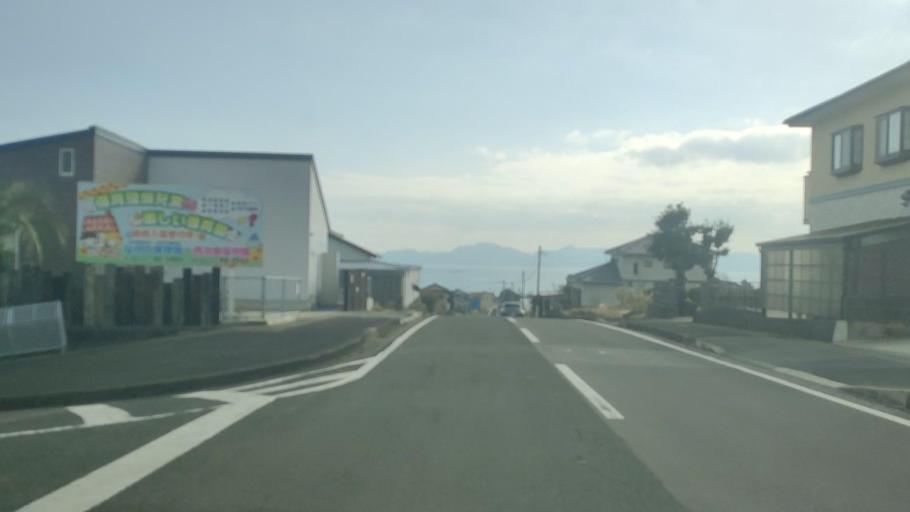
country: JP
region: Nagasaki
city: Shimabara
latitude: 32.6621
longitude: 130.2877
